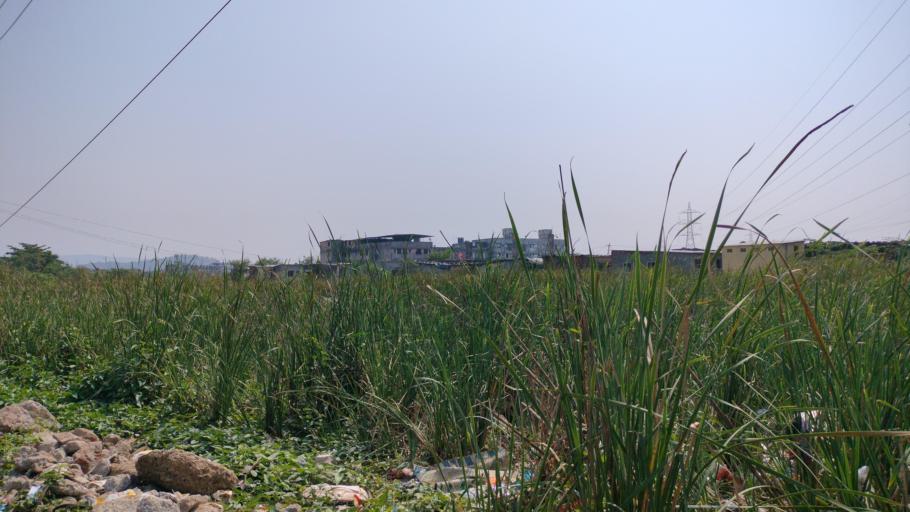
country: IN
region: Maharashtra
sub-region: Thane
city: Bhayandar
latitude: 19.3559
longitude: 72.8661
